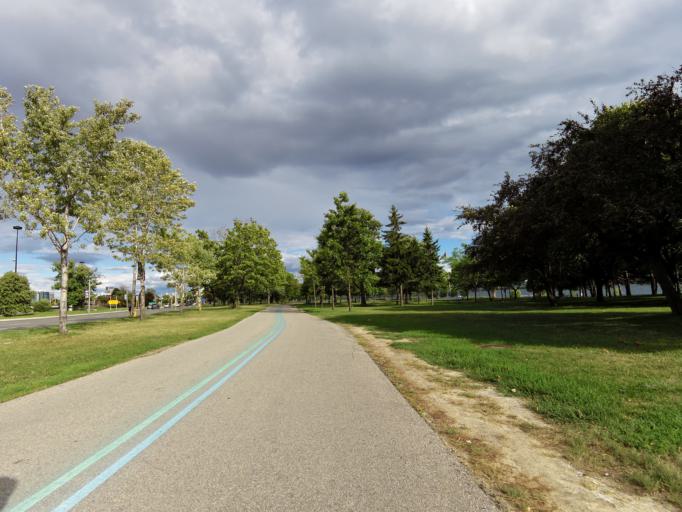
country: CA
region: Ontario
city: Toronto
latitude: 43.6320
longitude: -79.4345
